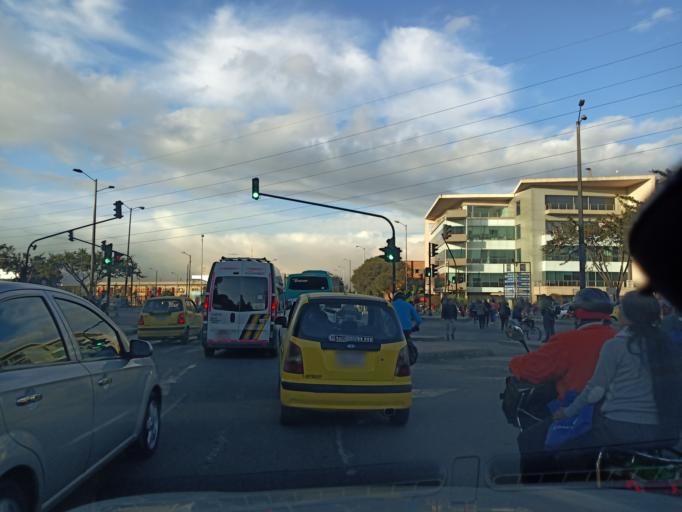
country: CO
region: Cundinamarca
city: Funza
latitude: 4.6743
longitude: -74.1526
